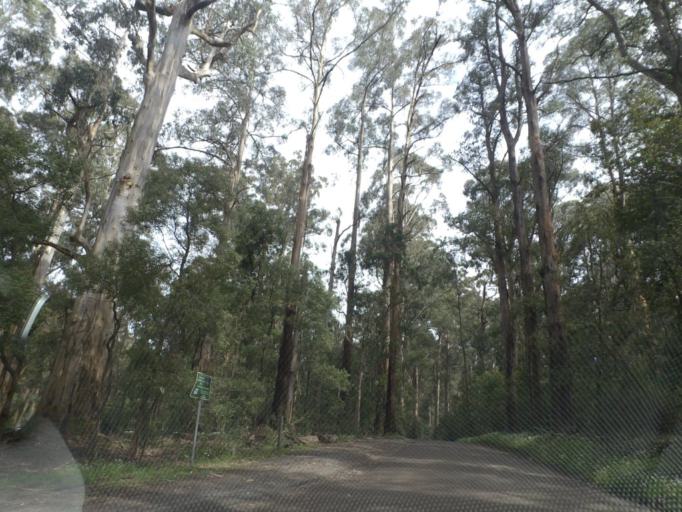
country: AU
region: Victoria
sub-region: Yarra Ranges
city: Mount Dandenong
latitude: -37.8339
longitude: 145.3698
